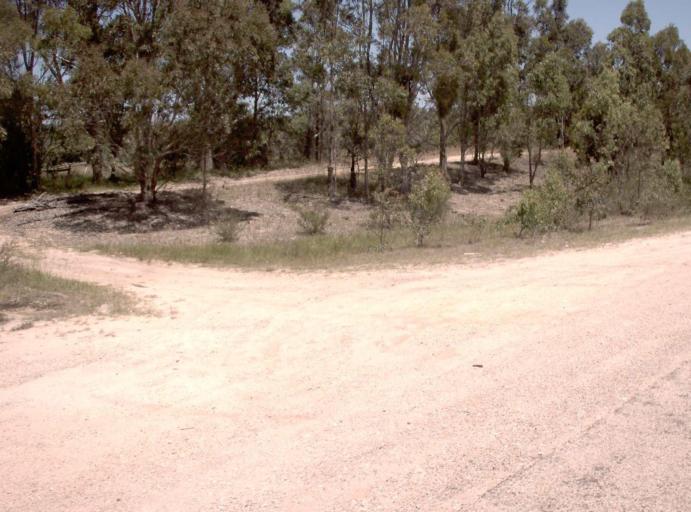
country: AU
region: Victoria
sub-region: East Gippsland
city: Bairnsdale
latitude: -37.7612
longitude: 147.7035
